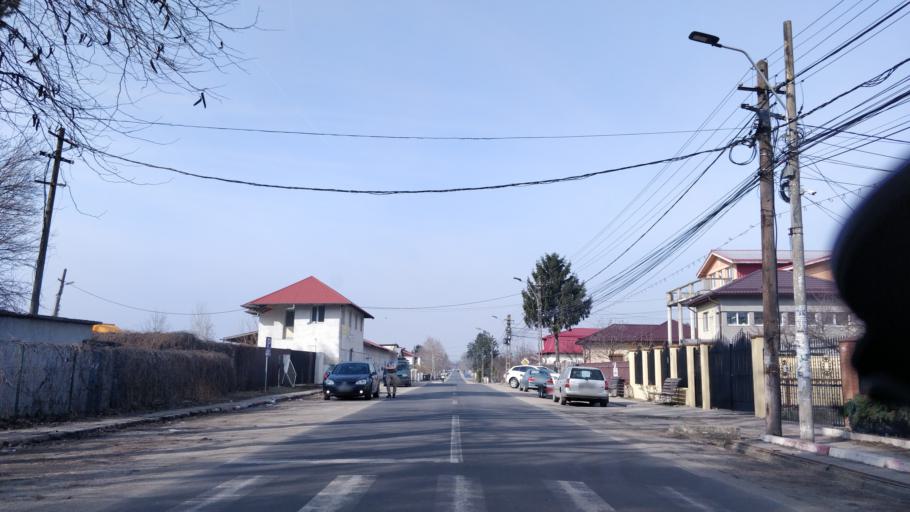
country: RO
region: Giurgiu
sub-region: Comuna Bolintin Deal
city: Bolintin Deal
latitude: 44.4541
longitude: 25.8228
